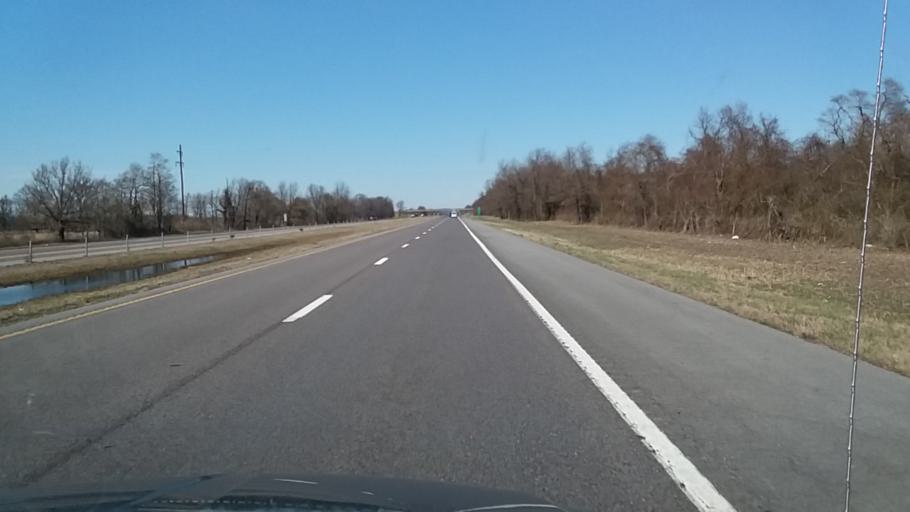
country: US
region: Missouri
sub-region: Scott County
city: Benton
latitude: 37.0327
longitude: -89.5352
